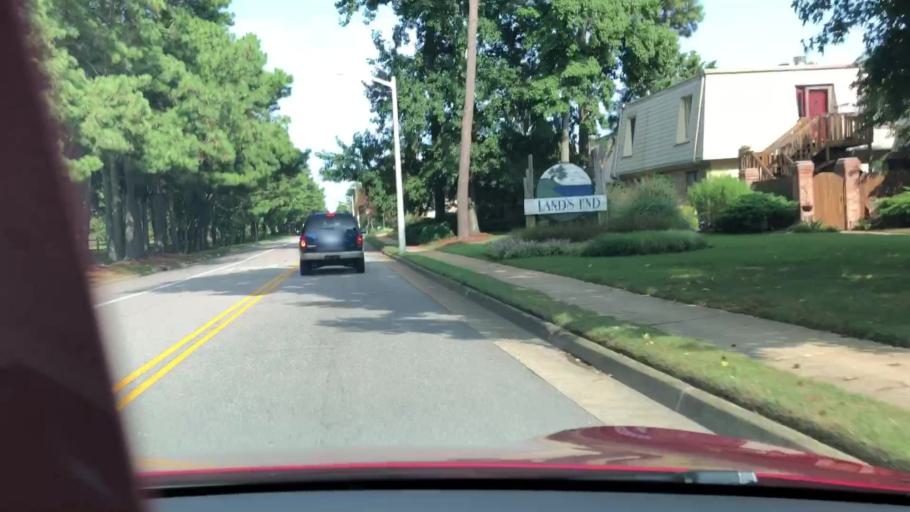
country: US
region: Virginia
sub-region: City of Virginia Beach
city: Virginia Beach
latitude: 36.8378
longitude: -75.9913
